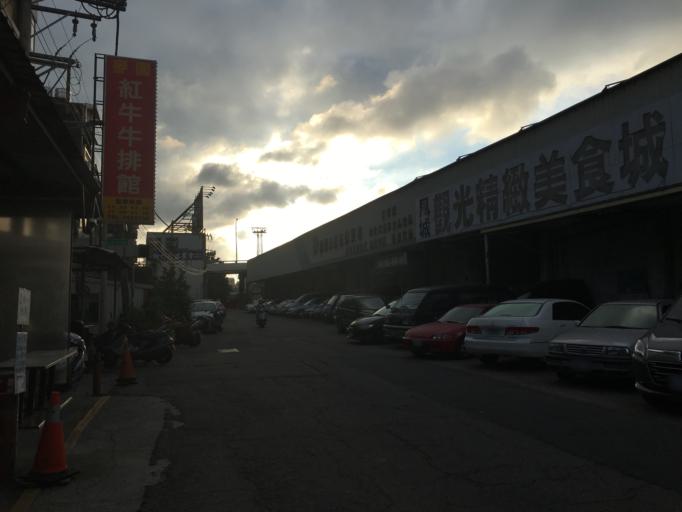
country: TW
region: Taiwan
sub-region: Hsinchu
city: Hsinchu
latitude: 24.8037
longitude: 120.9764
